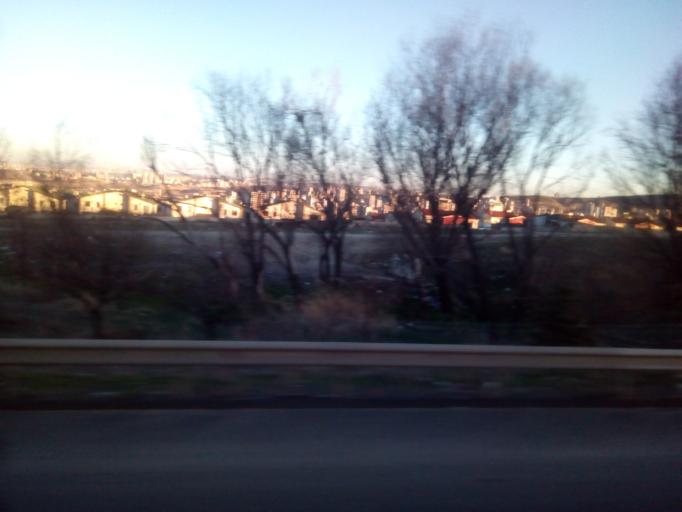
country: TR
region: Ankara
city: Etimesgut
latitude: 39.9098
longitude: 32.6292
